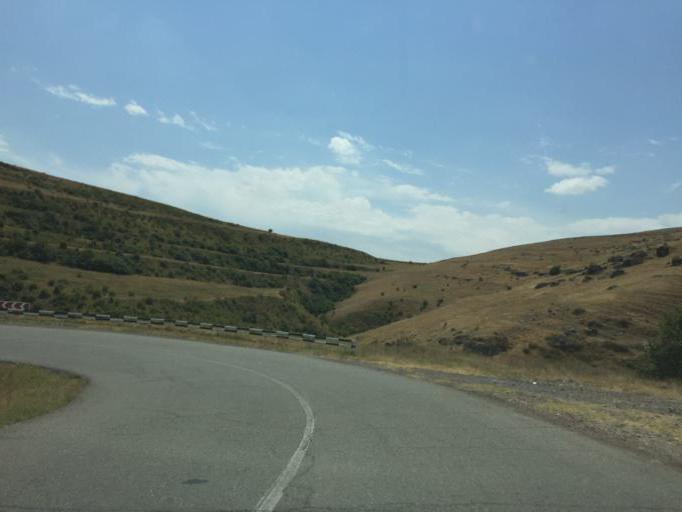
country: AZ
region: Lacin
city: Lacin
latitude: 39.5829
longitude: 46.5275
